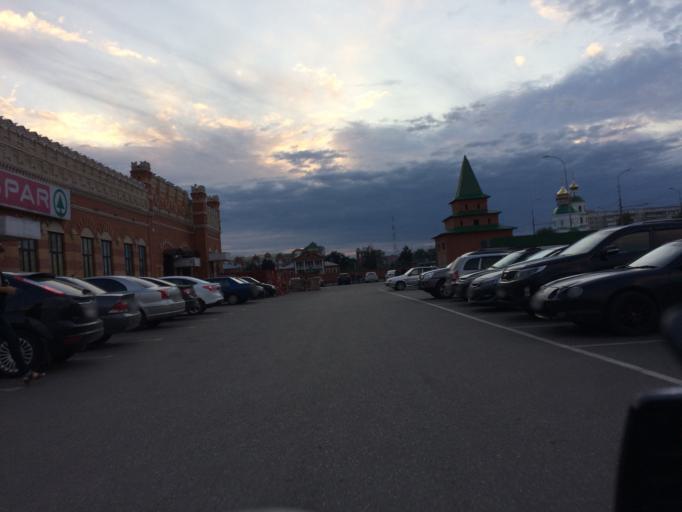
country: RU
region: Mariy-El
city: Yoshkar-Ola
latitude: 56.6377
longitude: 47.9077
